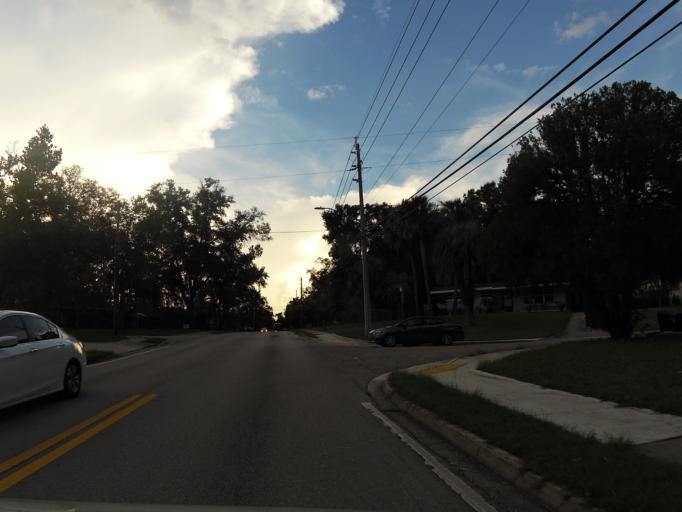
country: US
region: Florida
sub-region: Clay County
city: Bellair-Meadowbrook Terrace
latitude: 30.2812
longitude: -81.7814
